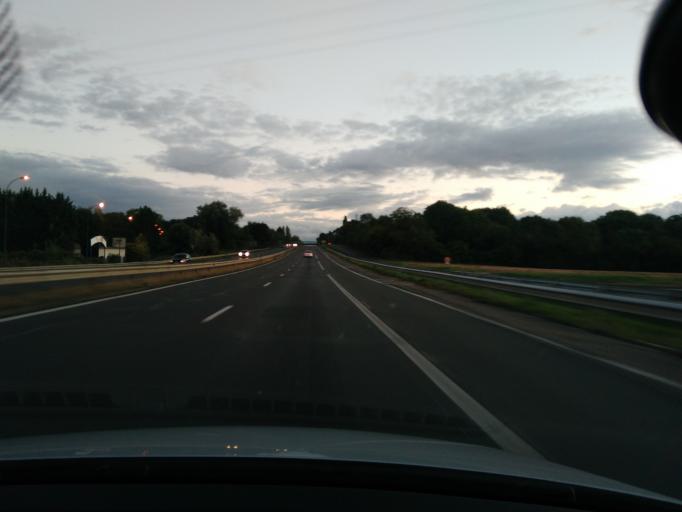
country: FR
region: Ile-de-France
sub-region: Departement de Seine-et-Marne
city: Nanteuil-les-Meaux
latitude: 48.9337
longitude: 2.8800
